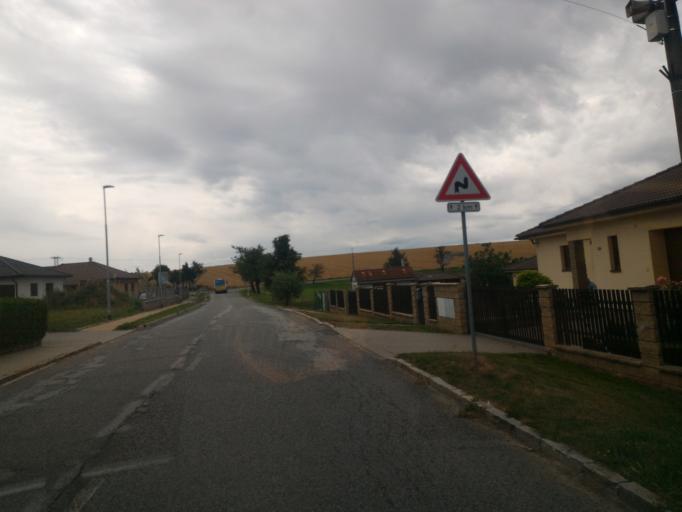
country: CZ
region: Vysocina
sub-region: Okres Jihlava
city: Trest'
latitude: 49.2408
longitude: 15.5608
